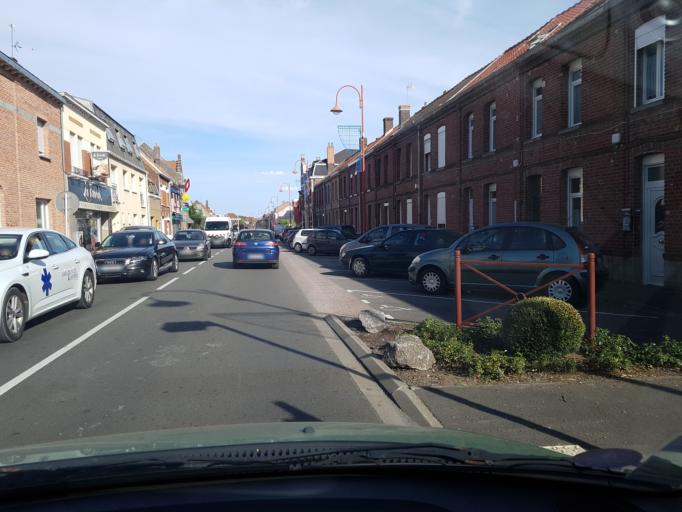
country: FR
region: Nord-Pas-de-Calais
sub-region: Departement du Pas-de-Calais
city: Annezin
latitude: 50.5393
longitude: 2.6217
